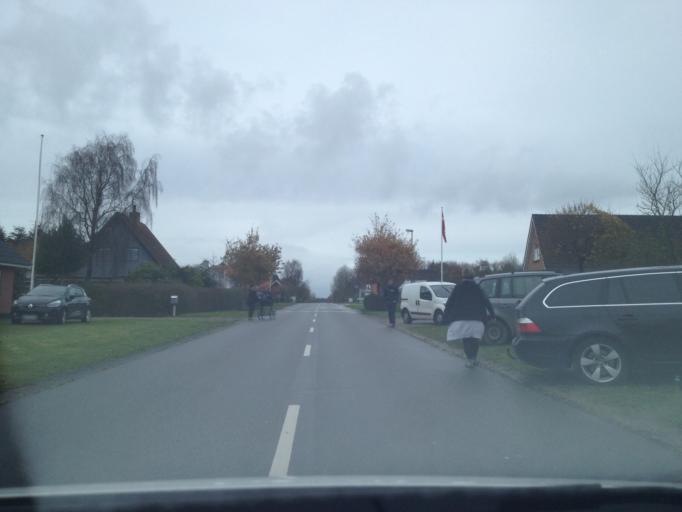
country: DK
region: South Denmark
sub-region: Esbjerg Kommune
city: Ribe
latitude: 55.2491
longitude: 8.8275
